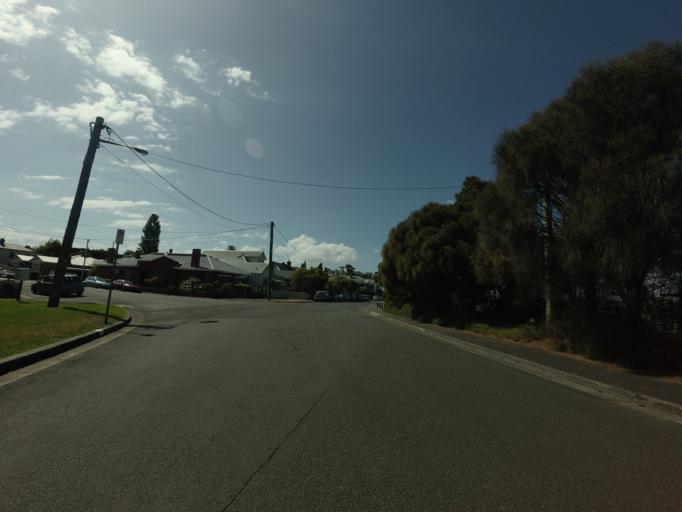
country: AU
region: Tasmania
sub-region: Hobart
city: Sandy Bay
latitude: -42.8969
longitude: 147.3320
